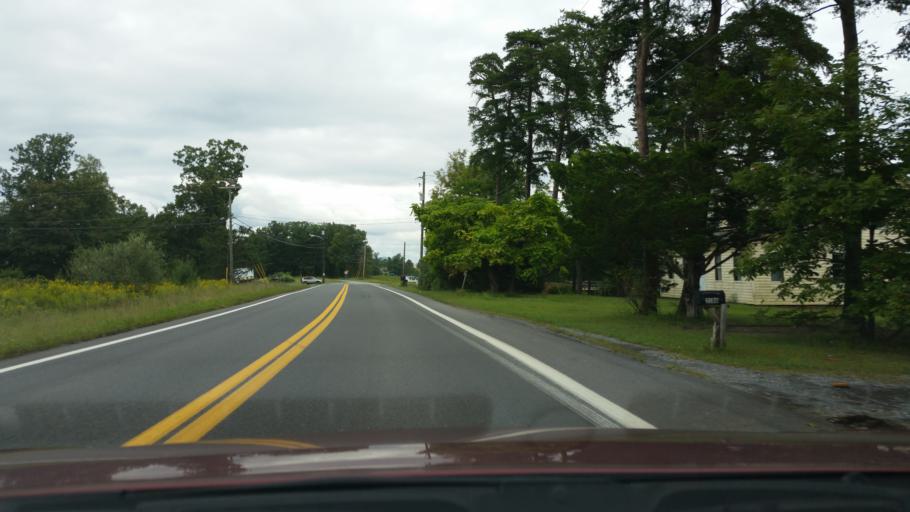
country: US
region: West Virginia
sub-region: Morgan County
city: Berkeley Springs
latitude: 39.6288
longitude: -78.1772
